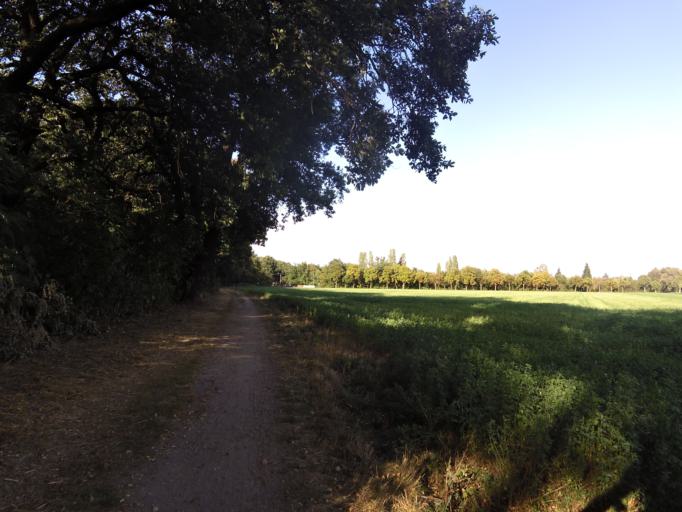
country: DE
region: Saxony
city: Schkeuditz
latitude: 51.3539
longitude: 12.2552
